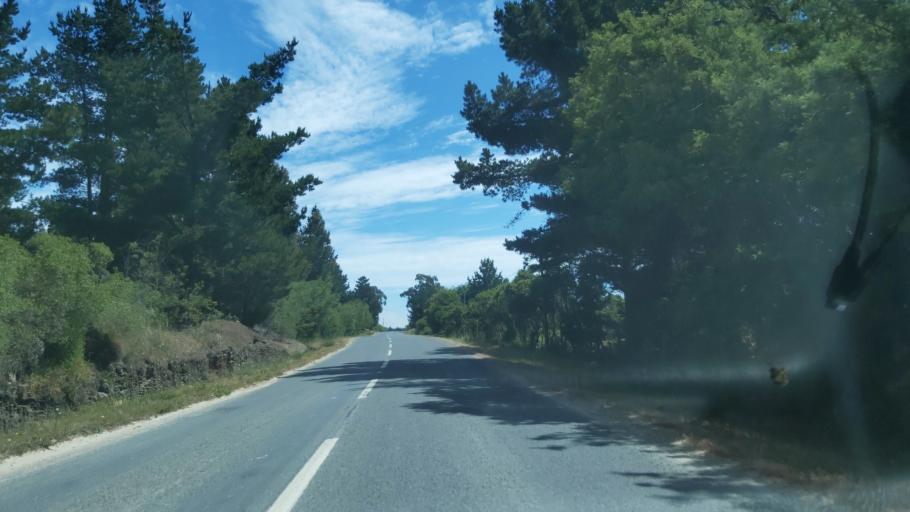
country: CL
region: Maule
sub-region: Provincia de Talca
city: Constitucion
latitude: -35.5623
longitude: -72.5908
